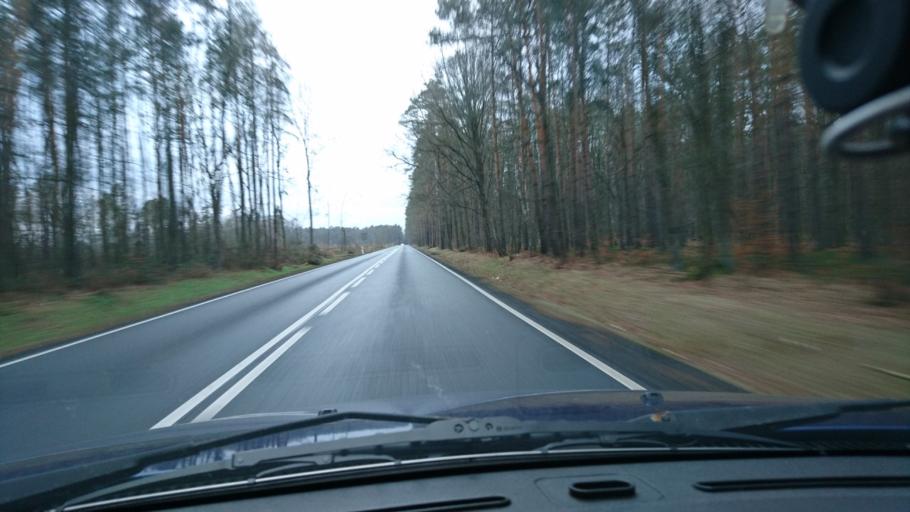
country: PL
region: Opole Voivodeship
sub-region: Powiat oleski
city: Olesno
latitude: 50.9380
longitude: 18.3287
